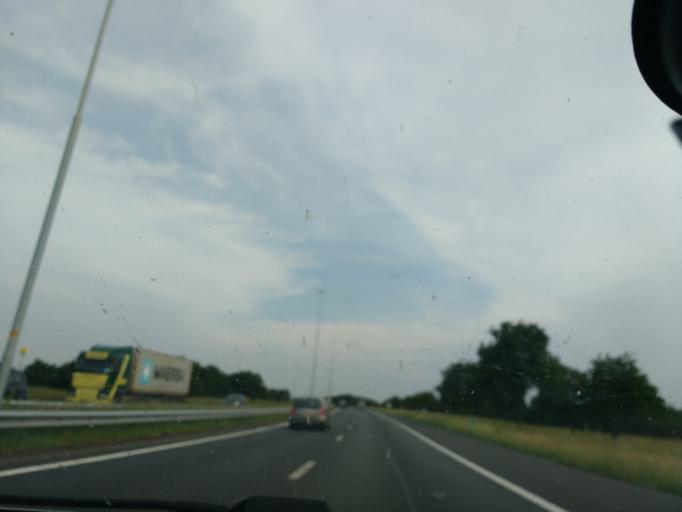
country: NL
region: North Brabant
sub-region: Gemeente Cuijk
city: Cuijk
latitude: 51.7336
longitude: 5.8467
